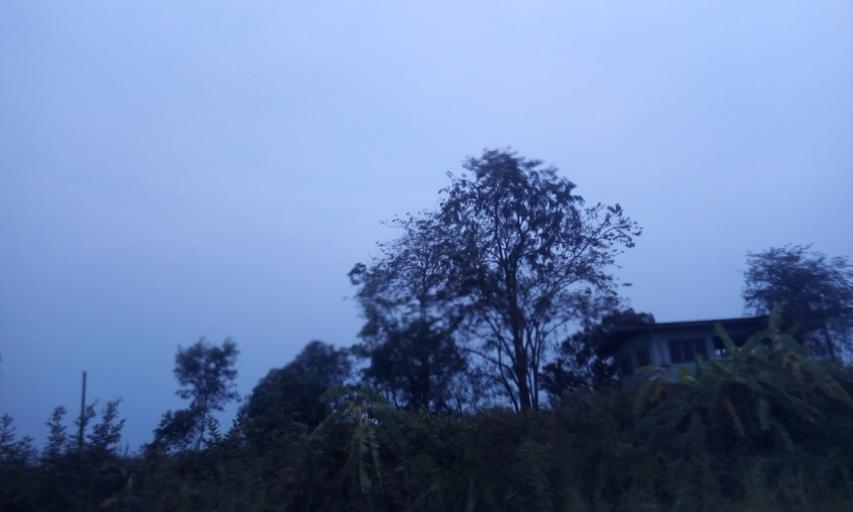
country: TH
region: Chachoengsao
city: Ban Pho
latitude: 13.5993
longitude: 101.1728
